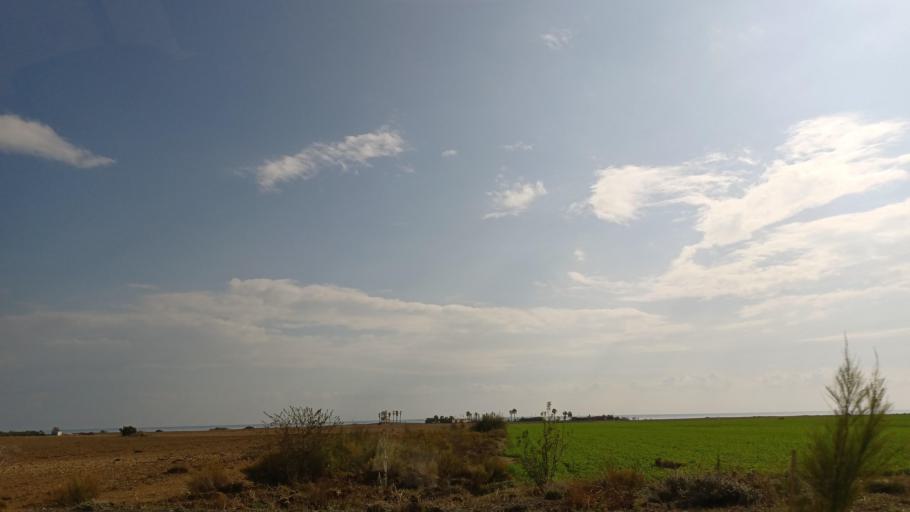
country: CY
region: Larnaka
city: Tersefanou
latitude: 34.8212
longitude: 33.5439
